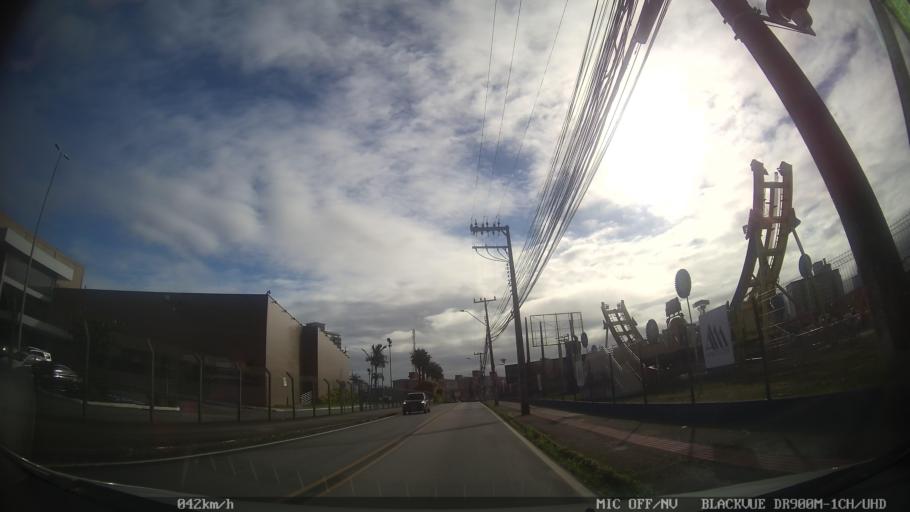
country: BR
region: Santa Catarina
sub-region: Sao Jose
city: Campinas
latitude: -27.5850
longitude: -48.6131
